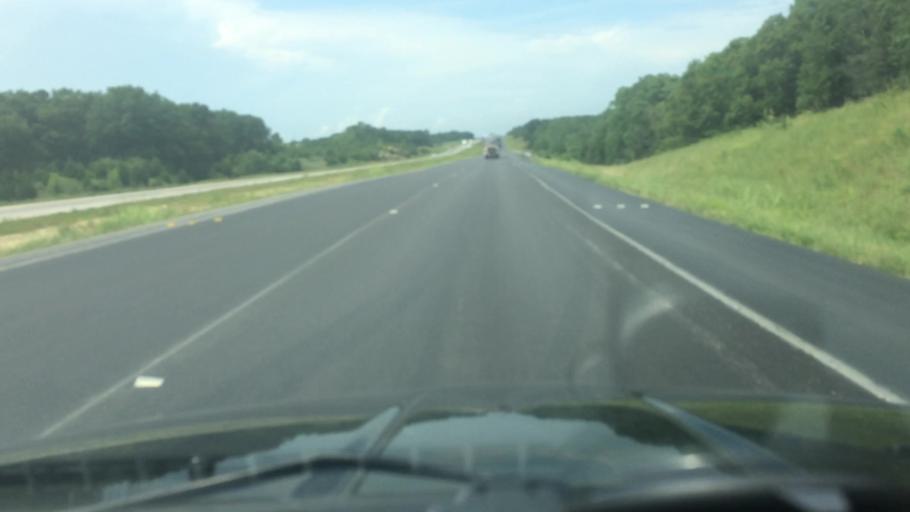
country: US
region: Missouri
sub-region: Saint Clair County
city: Osceola
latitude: 37.9550
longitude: -93.6417
